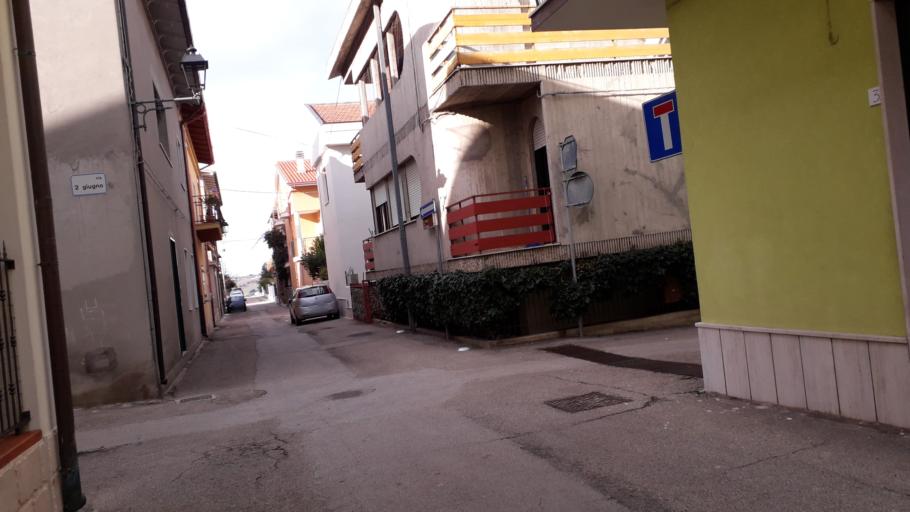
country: IT
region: Molise
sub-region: Provincia di Campobasso
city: Campomarino
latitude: 41.9572
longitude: 15.0324
